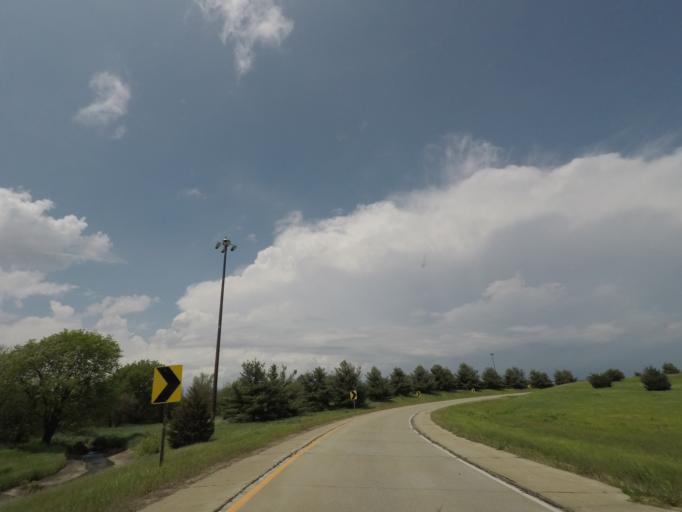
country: US
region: Illinois
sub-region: McLean County
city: Normal
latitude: 40.5364
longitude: -89.0092
